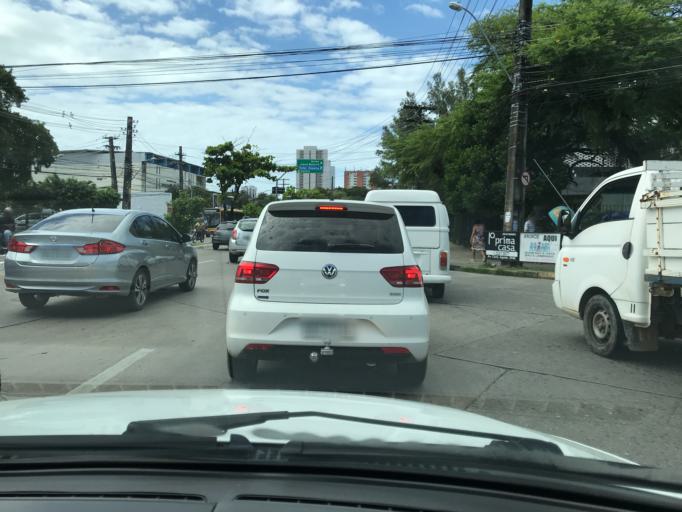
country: BR
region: Pernambuco
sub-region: Recife
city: Recife
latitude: -8.0612
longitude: -34.9047
